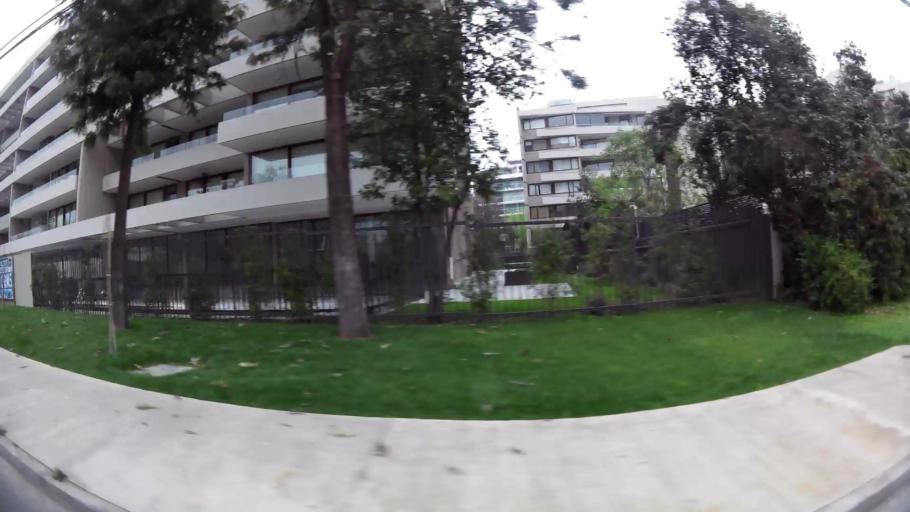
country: CL
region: Santiago Metropolitan
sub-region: Provincia de Santiago
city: Villa Presidente Frei, Nunoa, Santiago, Chile
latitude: -33.3997
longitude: -70.5824
